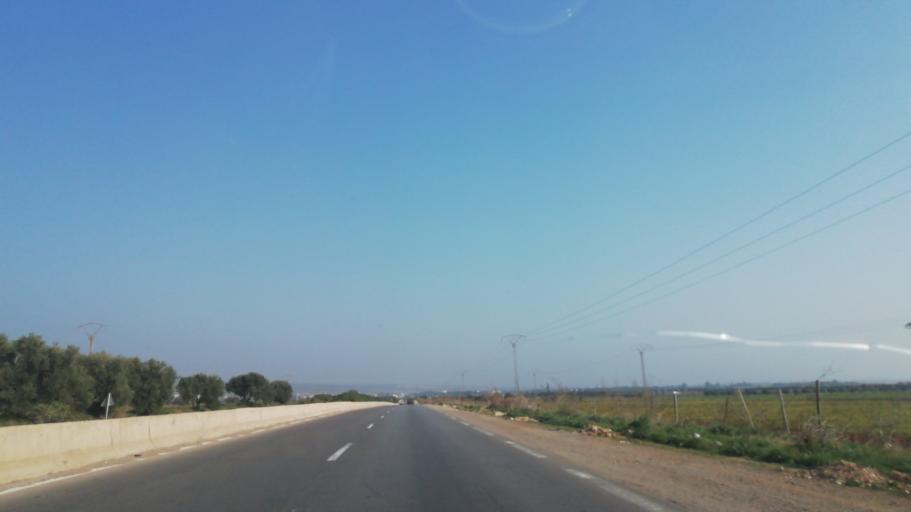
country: DZ
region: Oran
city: Bou Tlelis
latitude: 35.5611
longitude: -0.9289
